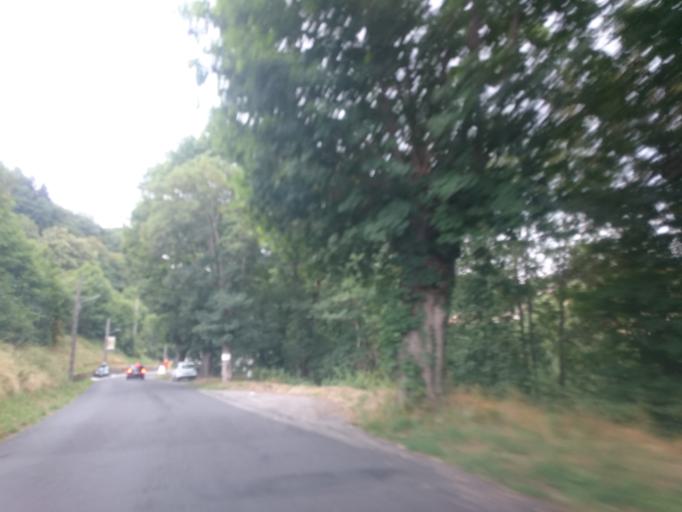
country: FR
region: Auvergne
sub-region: Departement du Cantal
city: Laroquebrou
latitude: 44.9653
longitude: 2.1923
